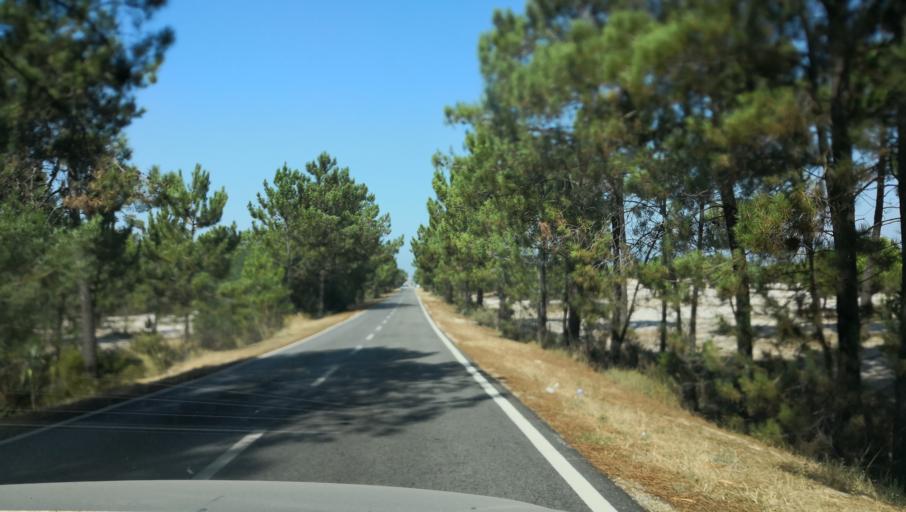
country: PT
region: Setubal
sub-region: Setubal
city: Setubal
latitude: 38.4030
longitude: -8.7448
